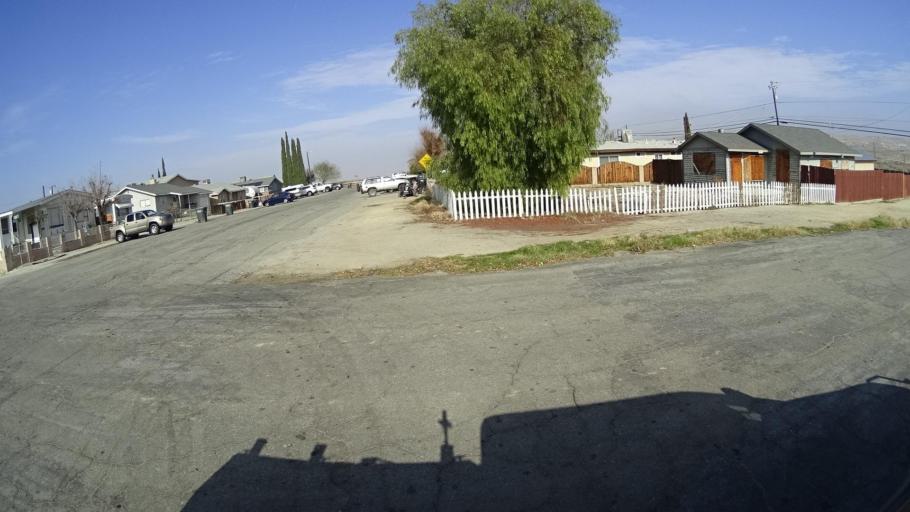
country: US
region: California
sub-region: Kern County
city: Ford City
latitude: 35.1576
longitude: -119.4524
